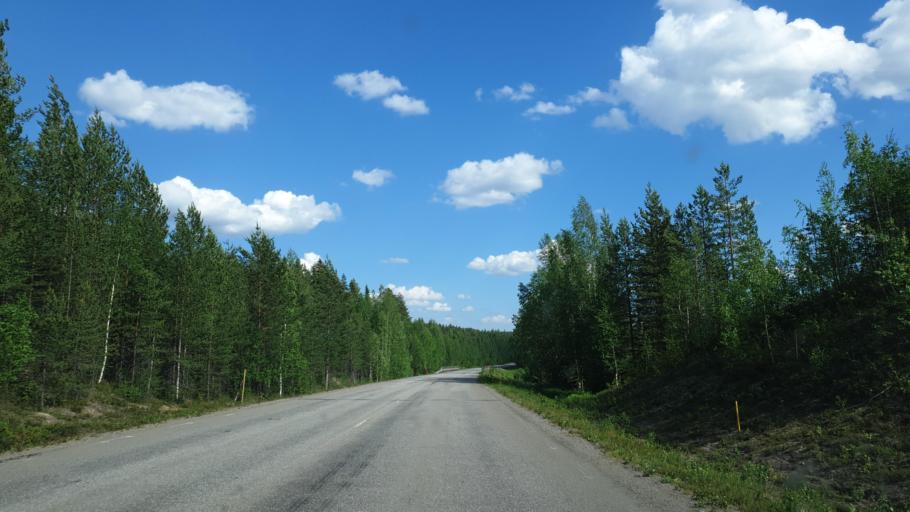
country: SE
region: Norrbotten
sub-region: Alvsbyns Kommun
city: AElvsbyn
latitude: 65.8336
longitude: 20.5324
